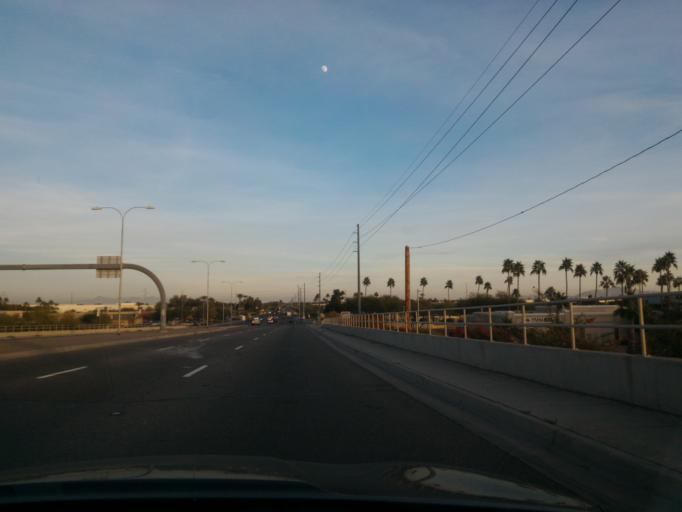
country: US
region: Arizona
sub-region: Maricopa County
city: Guadalupe
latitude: 33.3052
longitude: -111.9709
